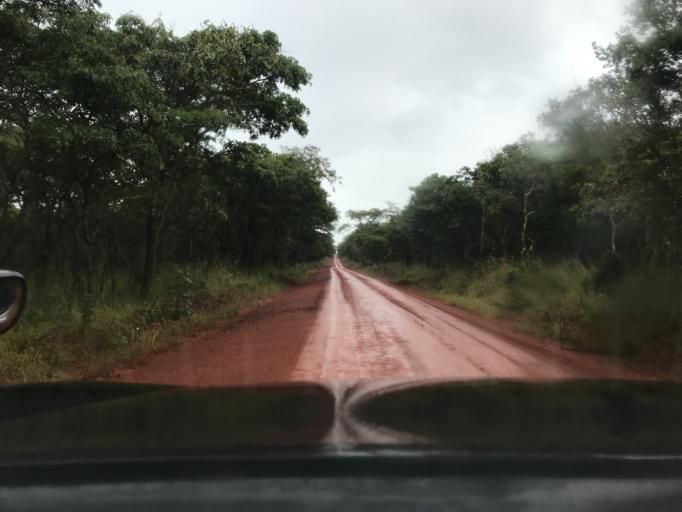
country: TZ
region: Kigoma
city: Uvinza
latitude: -5.2945
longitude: 30.3702
